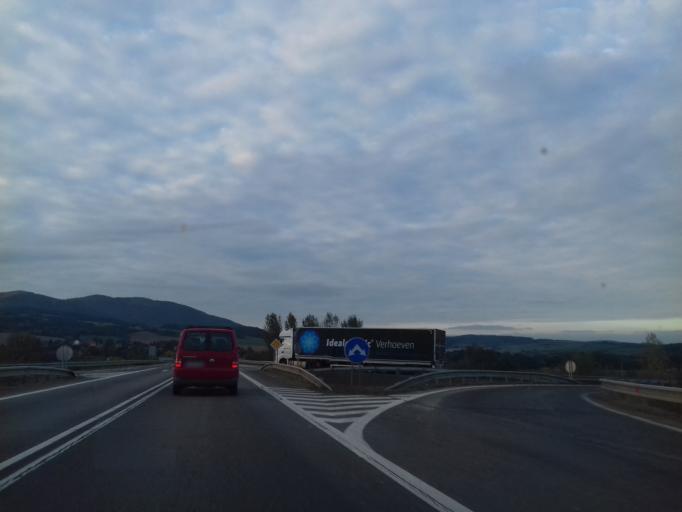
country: SK
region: Trenciansky
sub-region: Okres Trencin
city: Trencin
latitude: 48.8628
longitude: 17.9567
